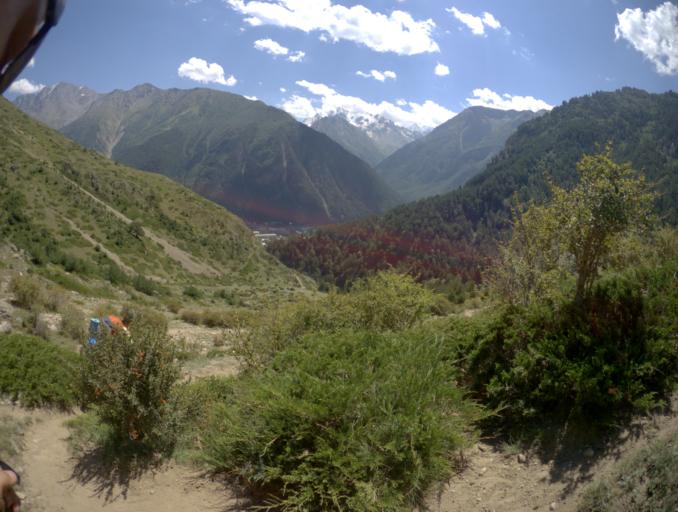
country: RU
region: Kabardino-Balkariya
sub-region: El'brusskiy Rayon
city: El'brus
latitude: 43.2661
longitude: 42.6348
